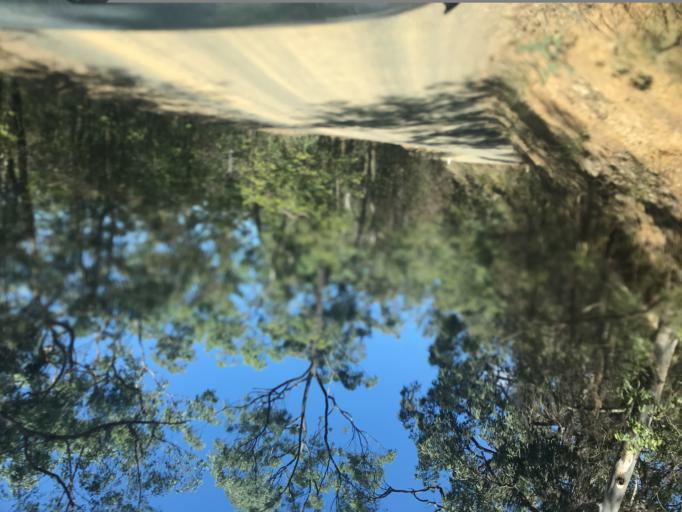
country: AU
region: New South Wales
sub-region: Wyong Shire
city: Little Jilliby
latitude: -33.1576
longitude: 151.0761
